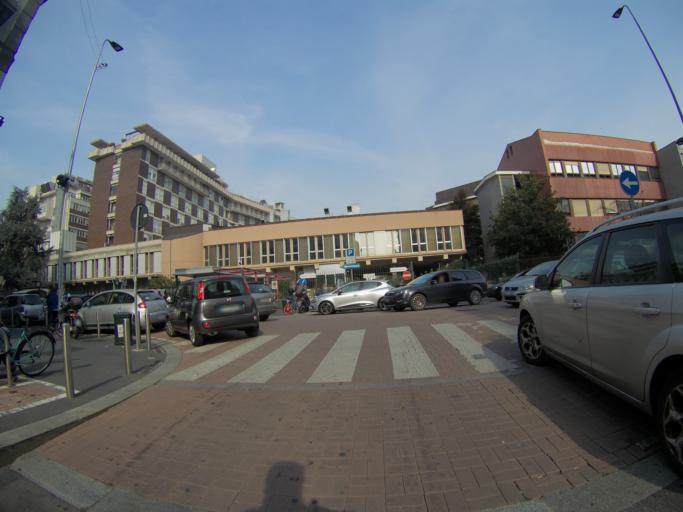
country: IT
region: Lombardy
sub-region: Citta metropolitana di Milano
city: Milano
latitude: 45.4741
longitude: 9.2324
